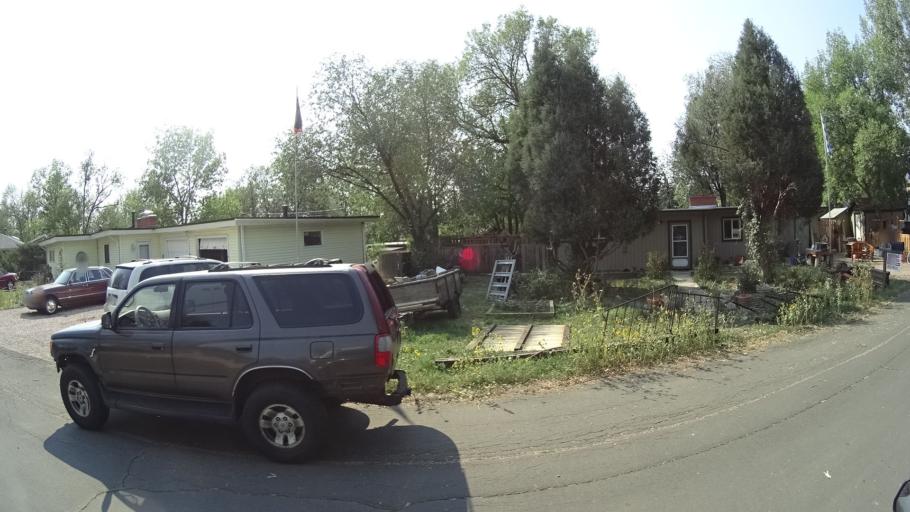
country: US
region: Colorado
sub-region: El Paso County
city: Colorado Springs
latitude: 38.8113
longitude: -104.8381
